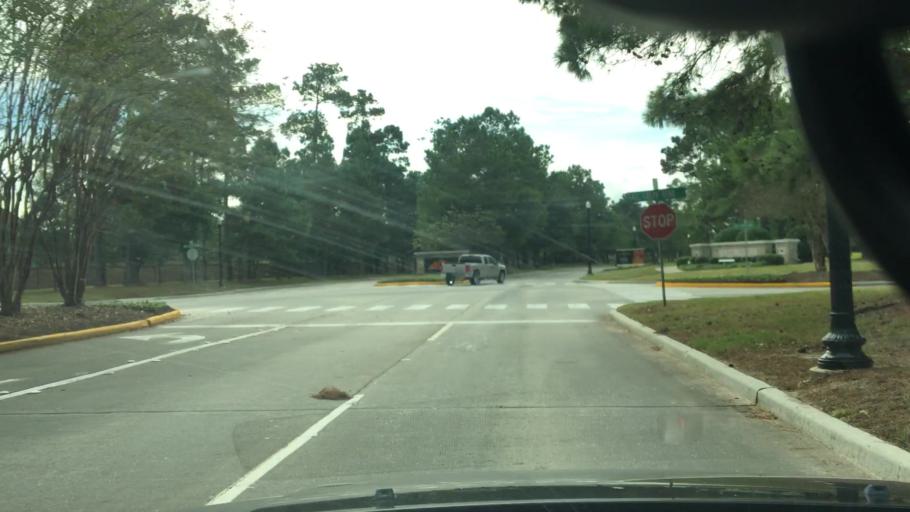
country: US
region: Texas
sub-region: Harris County
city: Humble
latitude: 29.9335
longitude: -95.2689
